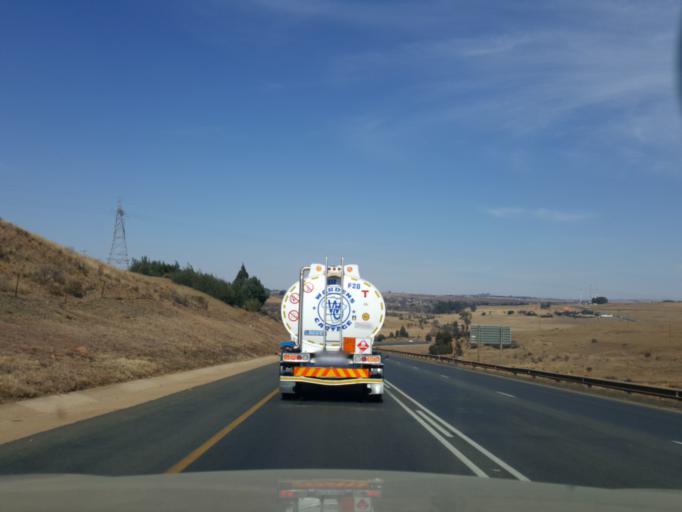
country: ZA
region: Mpumalanga
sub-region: Nkangala District Municipality
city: Belfast
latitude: -25.6395
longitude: 30.2524
